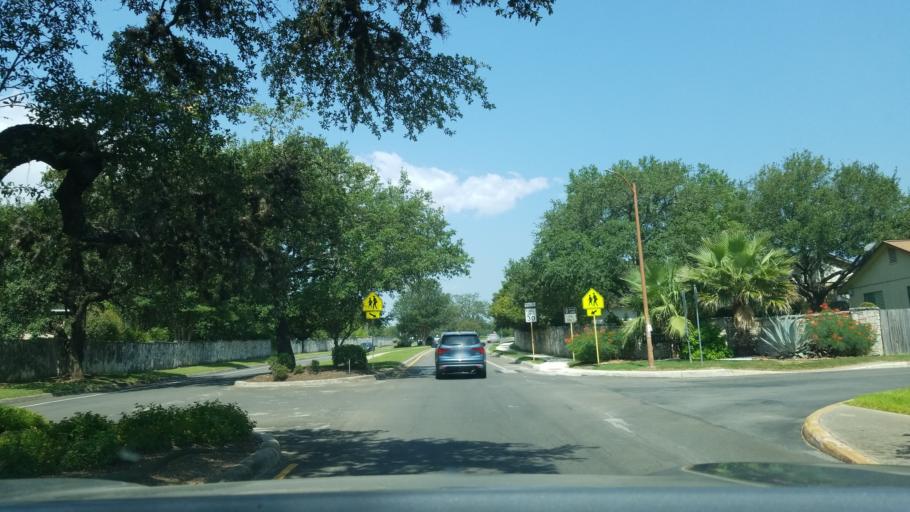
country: US
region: Texas
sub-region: Bexar County
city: Hollywood Park
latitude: 29.6298
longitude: -98.4514
